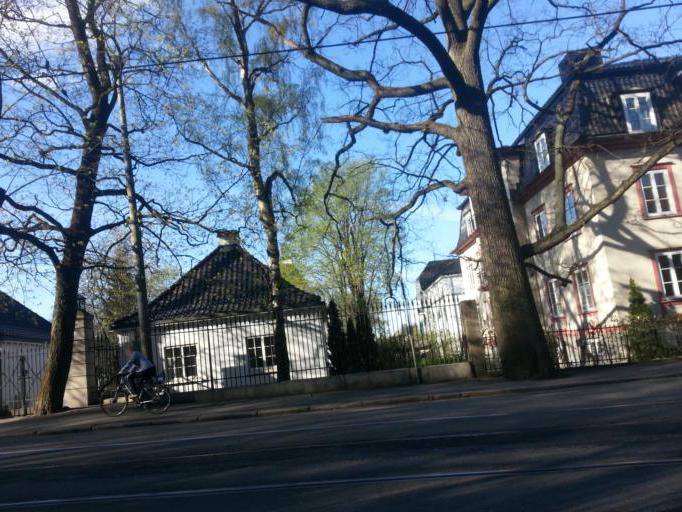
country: NO
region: Oslo
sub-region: Oslo
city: Sjolyststranda
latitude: 59.9140
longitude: 10.7034
